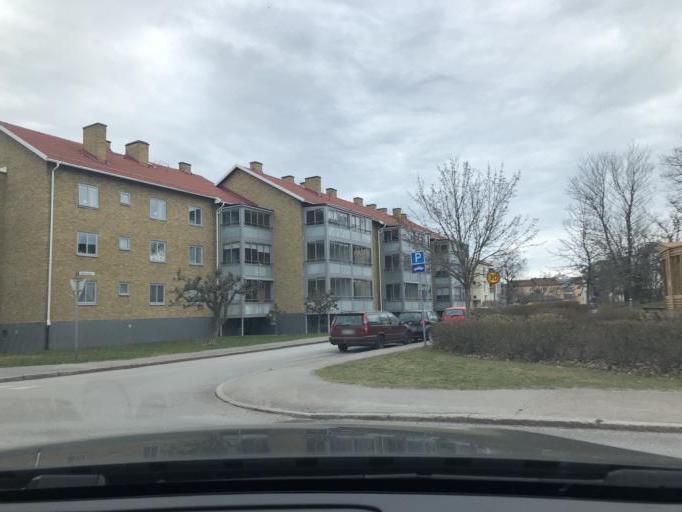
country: SE
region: Kalmar
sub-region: Kalmar Kommun
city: Kalmar
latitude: 56.6604
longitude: 16.3237
